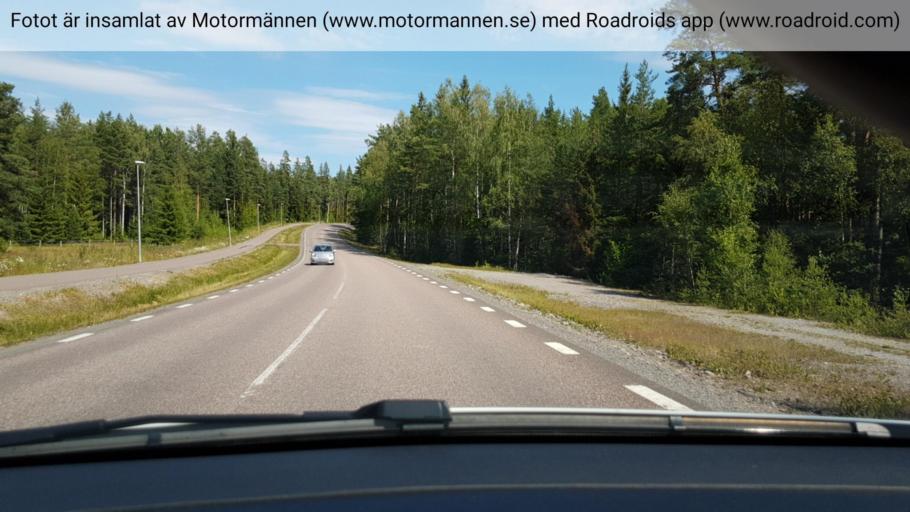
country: SE
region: Dalarna
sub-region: Faluns Kommun
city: Falun
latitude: 60.6001
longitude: 15.5456
